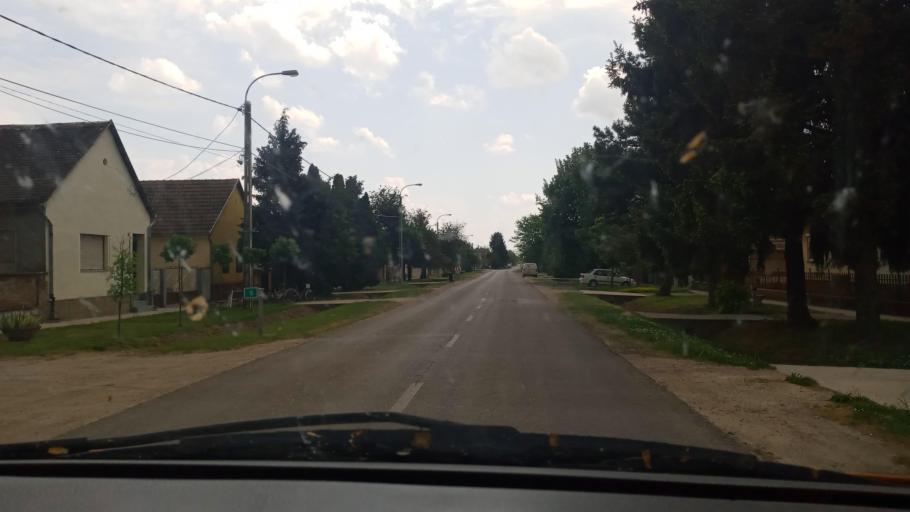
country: HU
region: Baranya
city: Beremend
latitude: 45.7815
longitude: 18.4367
